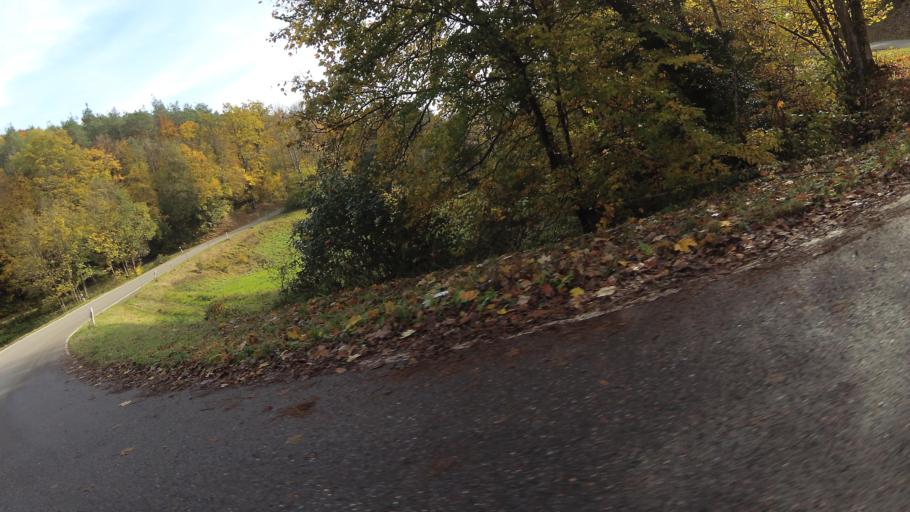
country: DE
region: Baden-Wuerttemberg
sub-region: Regierungsbezirk Stuttgart
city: Neudenau
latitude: 49.3171
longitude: 9.2977
